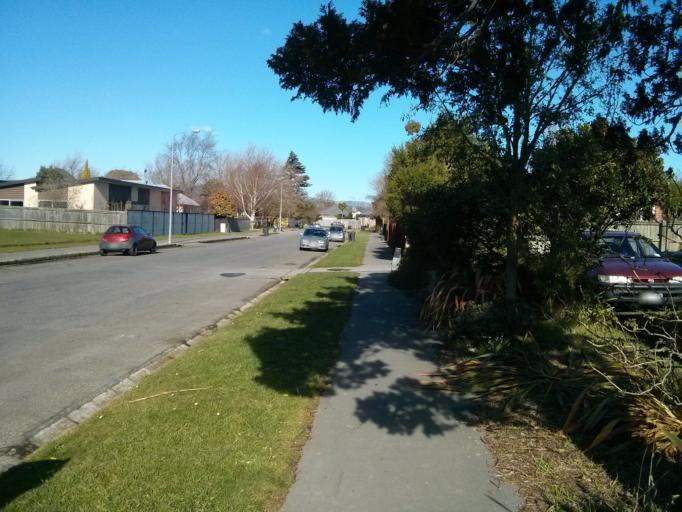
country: NZ
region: Canterbury
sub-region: Christchurch City
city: Christchurch
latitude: -43.5313
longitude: 172.5885
